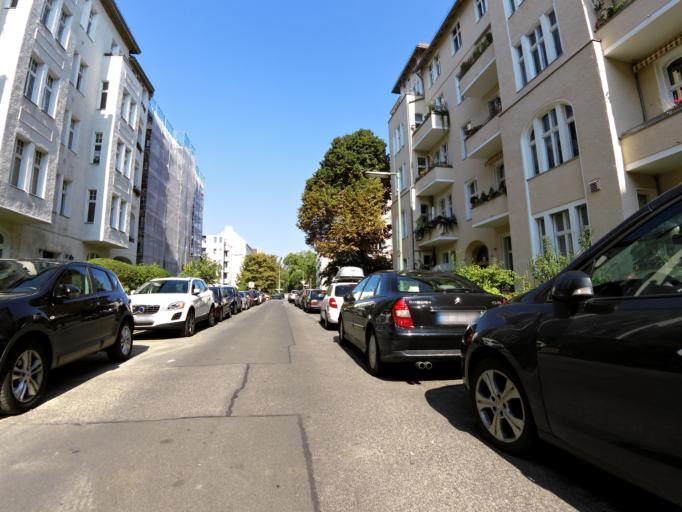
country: DE
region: Berlin
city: Berlin Schoeneberg
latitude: 52.4882
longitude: 13.3438
